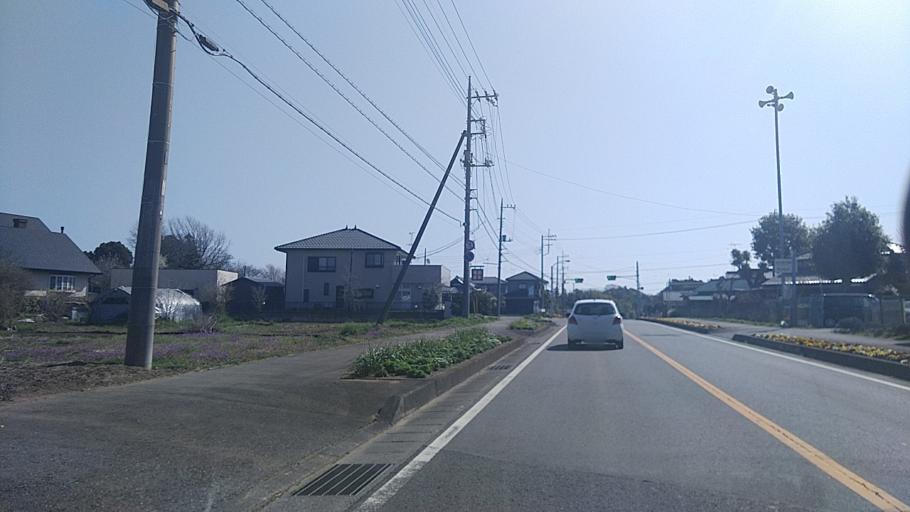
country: JP
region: Ibaraki
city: Toride
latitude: 35.8857
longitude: 140.1104
